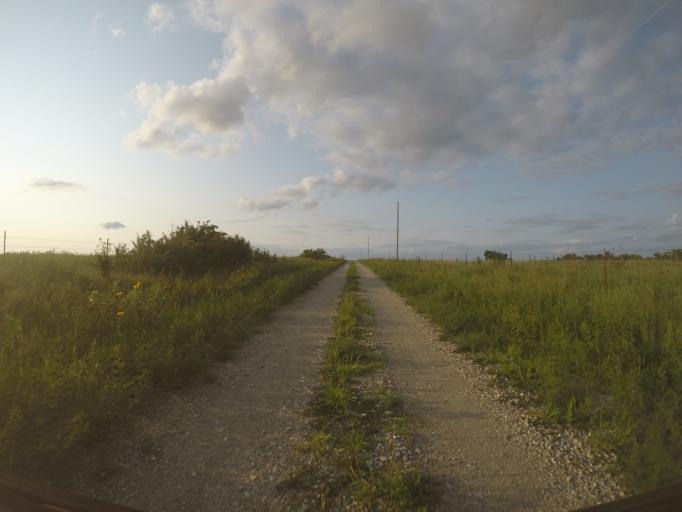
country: US
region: Kansas
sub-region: Wabaunsee County
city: Alma
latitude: 39.0779
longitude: -96.3773
